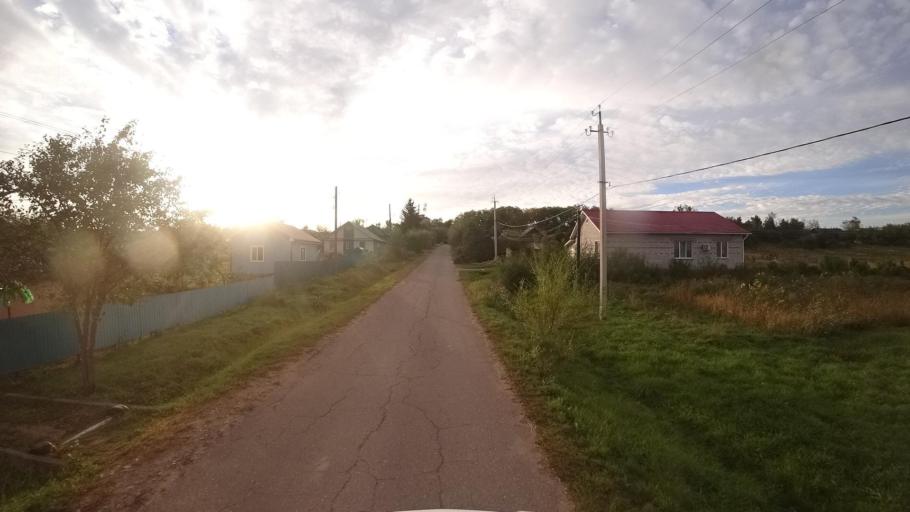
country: RU
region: Primorskiy
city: Yakovlevka
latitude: 44.4236
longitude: 133.4791
